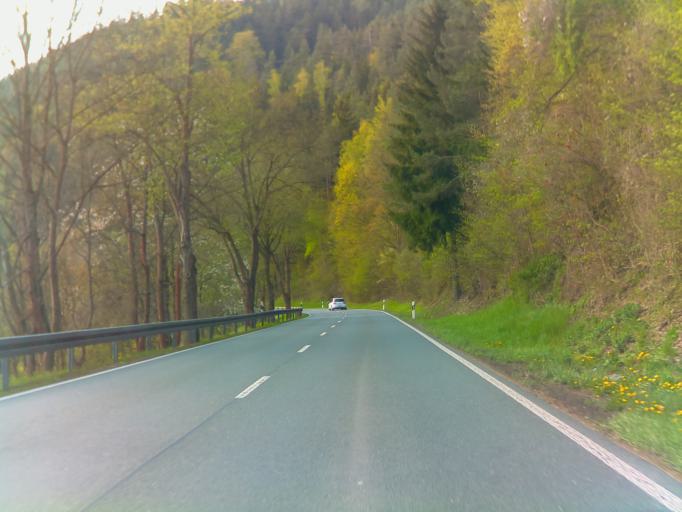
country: DE
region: Thuringia
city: Probstzella
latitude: 50.5428
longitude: 11.3687
